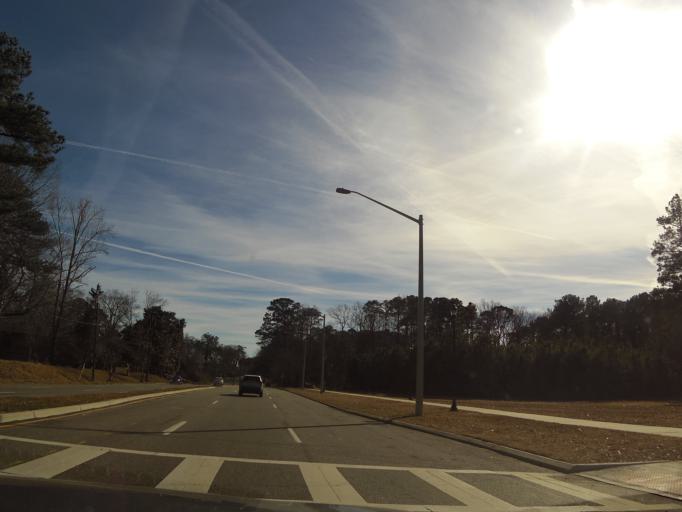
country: US
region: Virginia
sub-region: City of Newport News
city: Newport News
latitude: 37.0575
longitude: -76.4829
